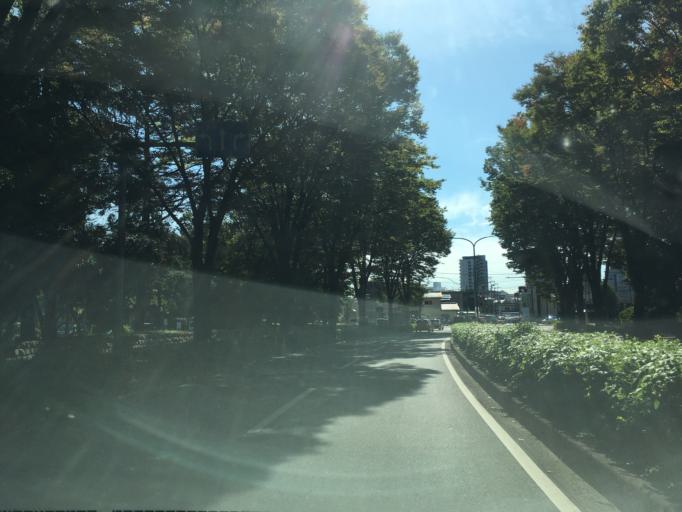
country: JP
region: Saitama
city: Tokorozawa
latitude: 35.7957
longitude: 139.4710
